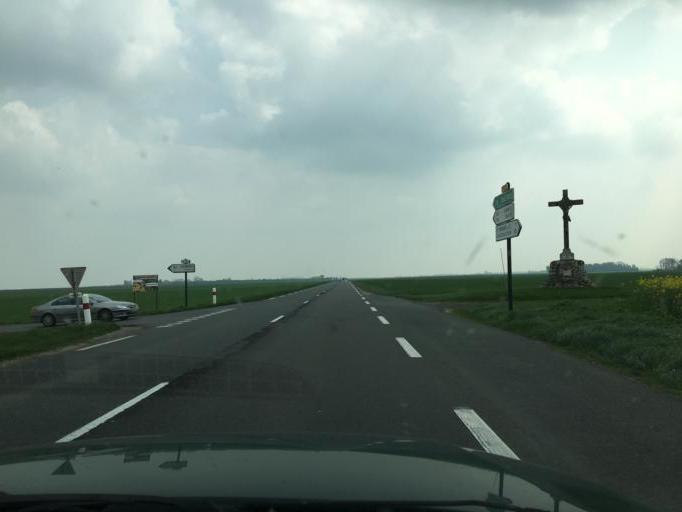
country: FR
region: Centre
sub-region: Departement du Loiret
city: Patay
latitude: 47.9949
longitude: 1.7140
